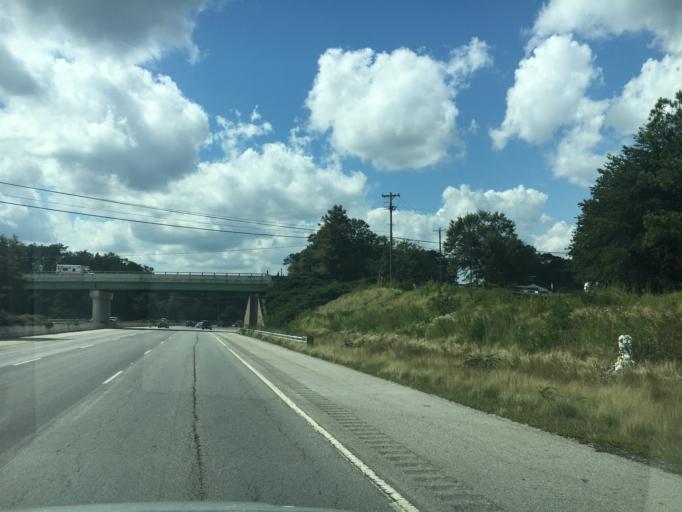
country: US
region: South Carolina
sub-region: Greenville County
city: Greenville
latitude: 34.8551
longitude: -82.3622
